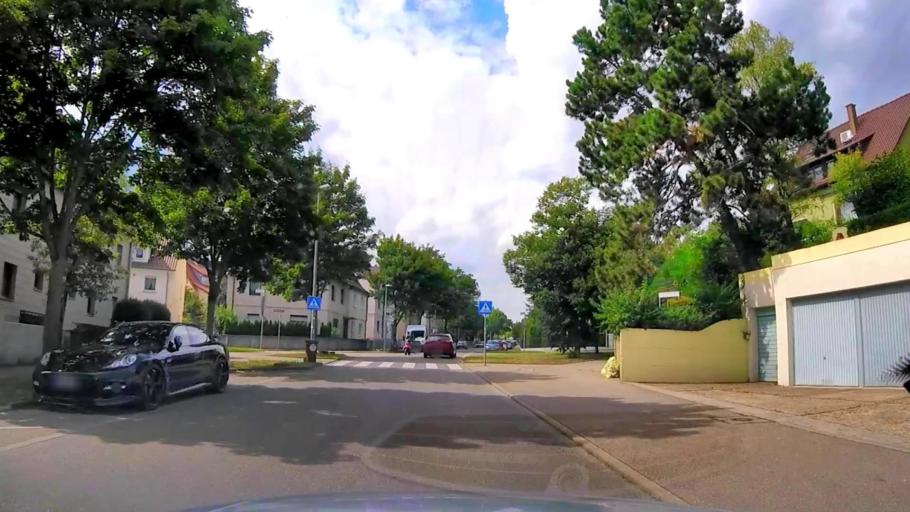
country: DE
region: Baden-Wuerttemberg
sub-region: Regierungsbezirk Stuttgart
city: Stuttgart Feuerbach
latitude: 48.8117
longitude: 9.1477
